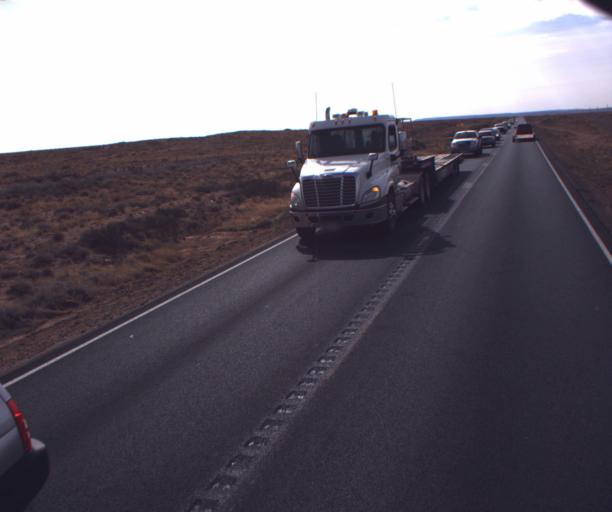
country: US
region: Arizona
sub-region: Apache County
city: Chinle
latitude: 36.0541
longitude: -109.6085
